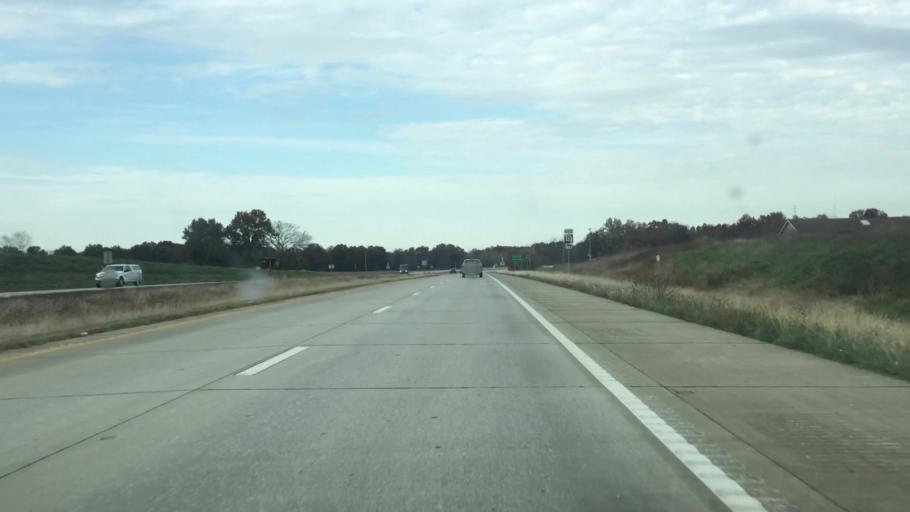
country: US
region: Missouri
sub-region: Henry County
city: Clinton
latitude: 38.3493
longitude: -93.7566
